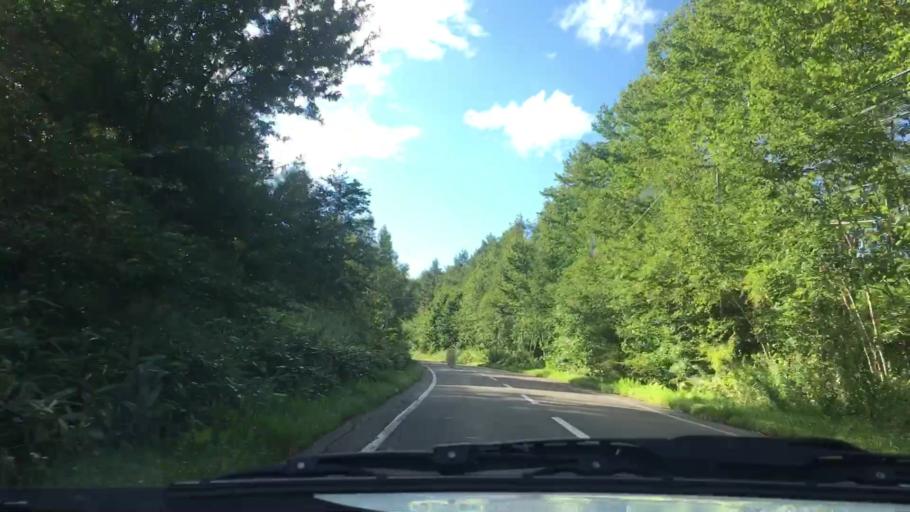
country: JP
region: Hokkaido
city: Otofuke
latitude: 43.1722
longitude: 142.9737
